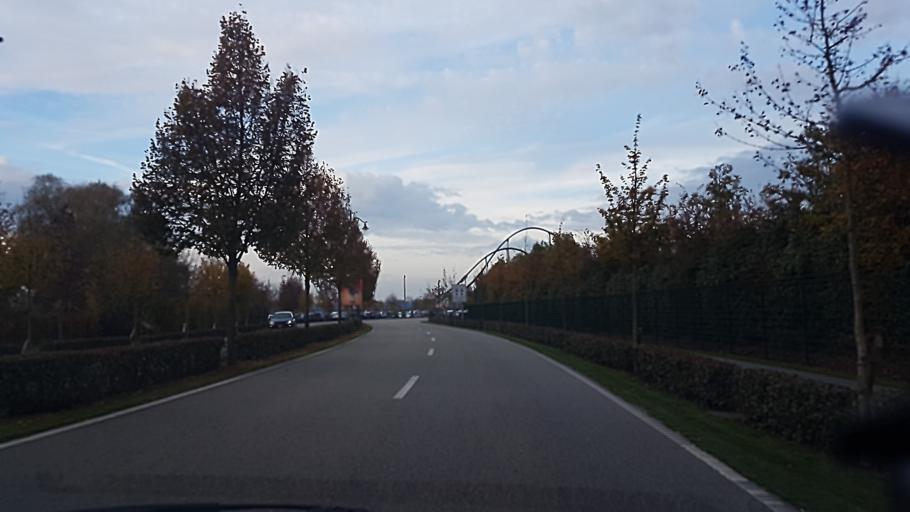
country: DE
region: Baden-Wuerttemberg
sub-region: Freiburg Region
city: Rust
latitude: 48.2659
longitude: 7.7164
